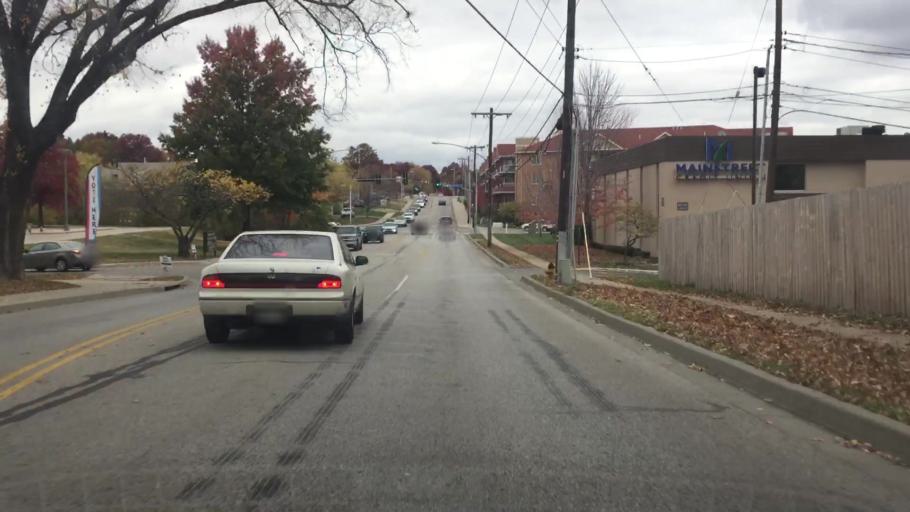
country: US
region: Kansas
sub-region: Johnson County
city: Mission
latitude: 39.0189
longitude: -94.6583
